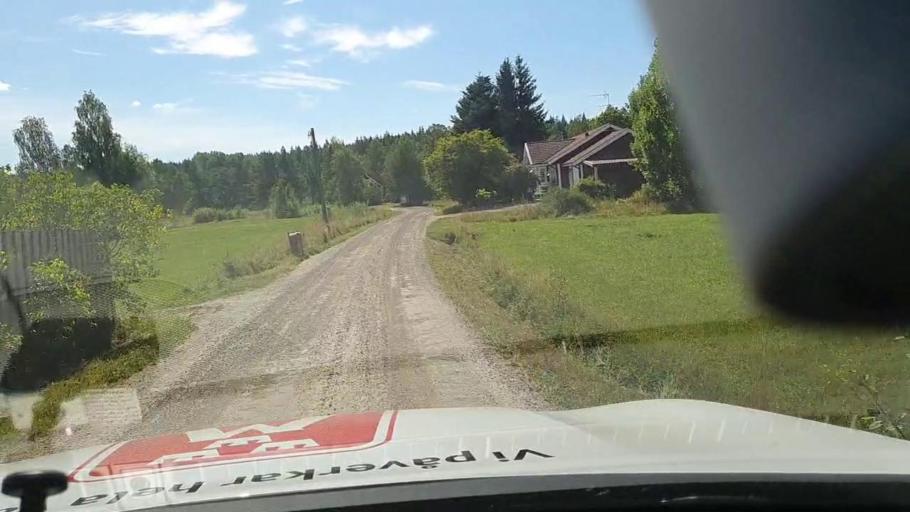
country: SE
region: Soedermanland
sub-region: Strangnas Kommun
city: Akers Styckebruk
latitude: 59.2143
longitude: 16.9100
